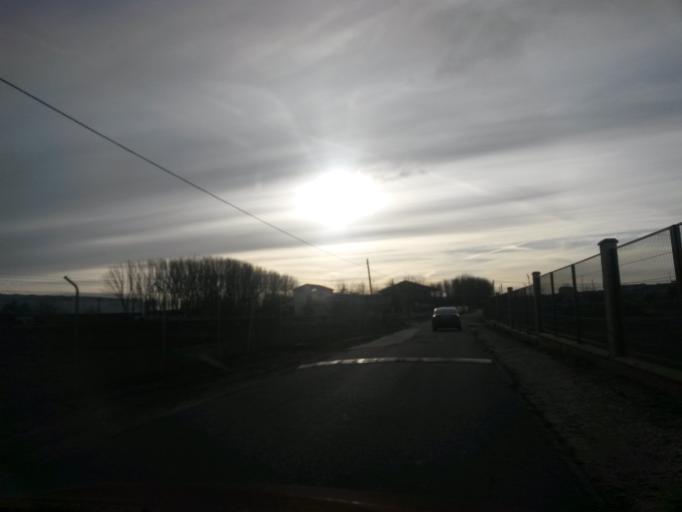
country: ES
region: Castille and Leon
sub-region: Provincia de Salamanca
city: Santa Marta de Tormes
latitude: 40.9647
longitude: -5.6341
